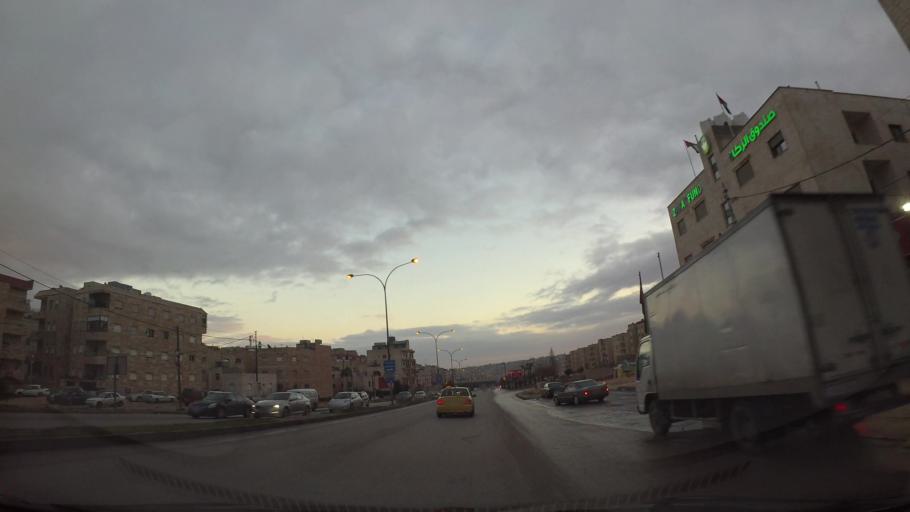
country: JO
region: Amman
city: Amman
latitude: 31.9869
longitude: 35.9180
